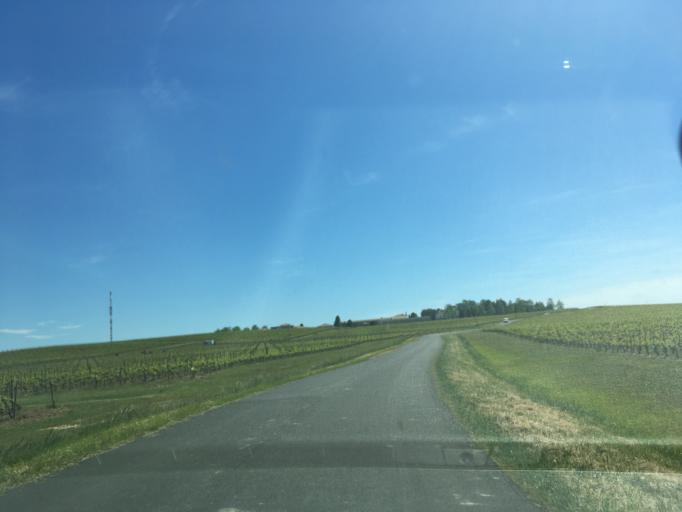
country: FR
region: Aquitaine
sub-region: Departement de la Gironde
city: Lesparre-Medoc
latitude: 45.3139
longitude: -0.8810
